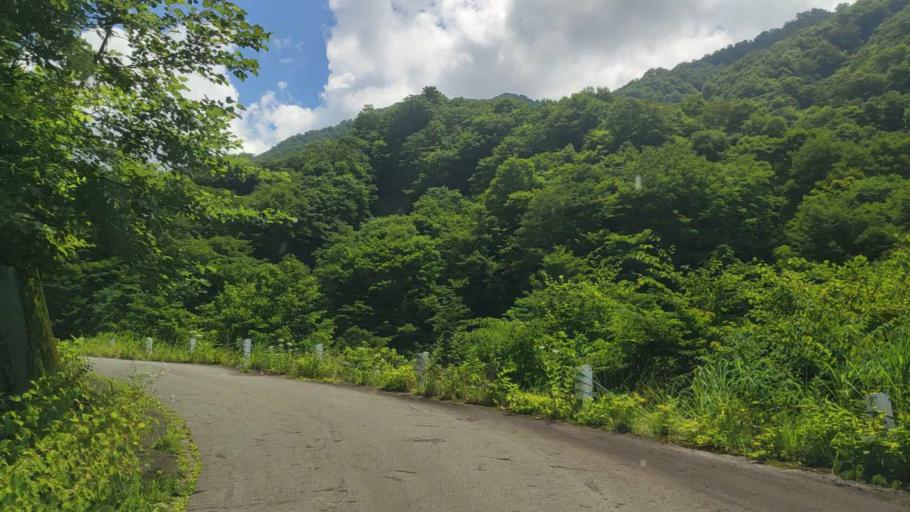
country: JP
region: Fukui
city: Ono
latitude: 35.7846
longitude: 136.5124
